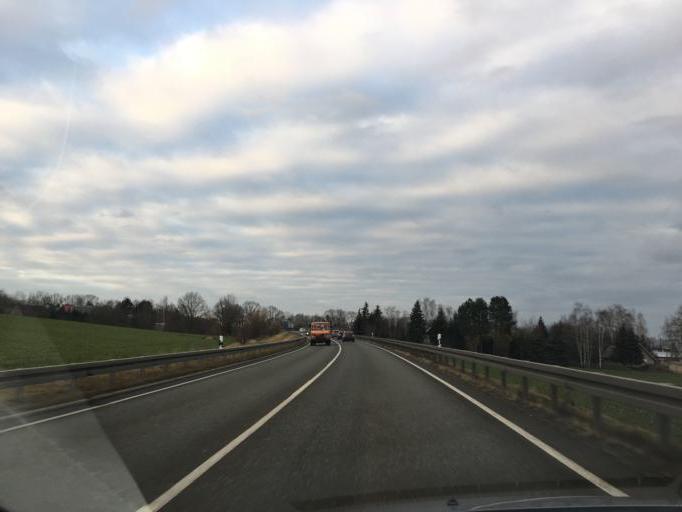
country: DE
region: Thuringia
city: Nobitz
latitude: 50.9988
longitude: 12.4708
